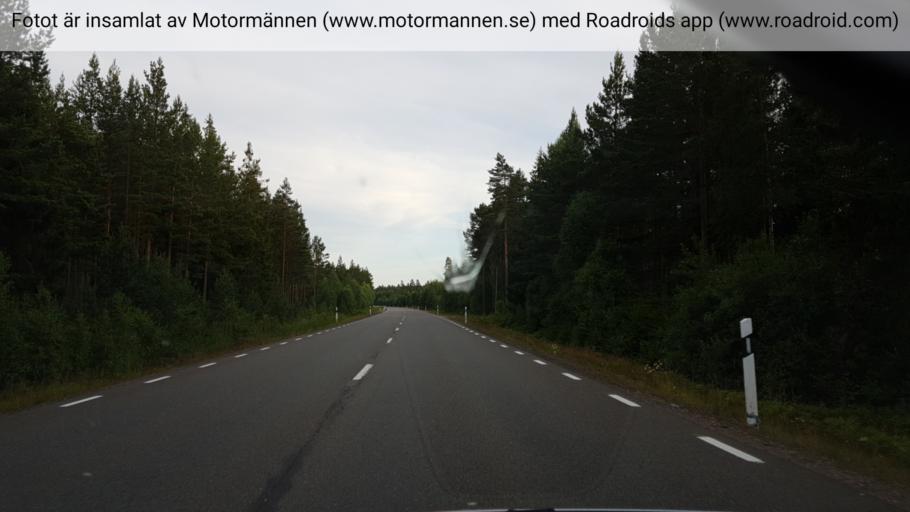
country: SE
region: Vaestra Goetaland
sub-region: Tibro Kommun
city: Tibro
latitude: 58.5318
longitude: 14.1508
